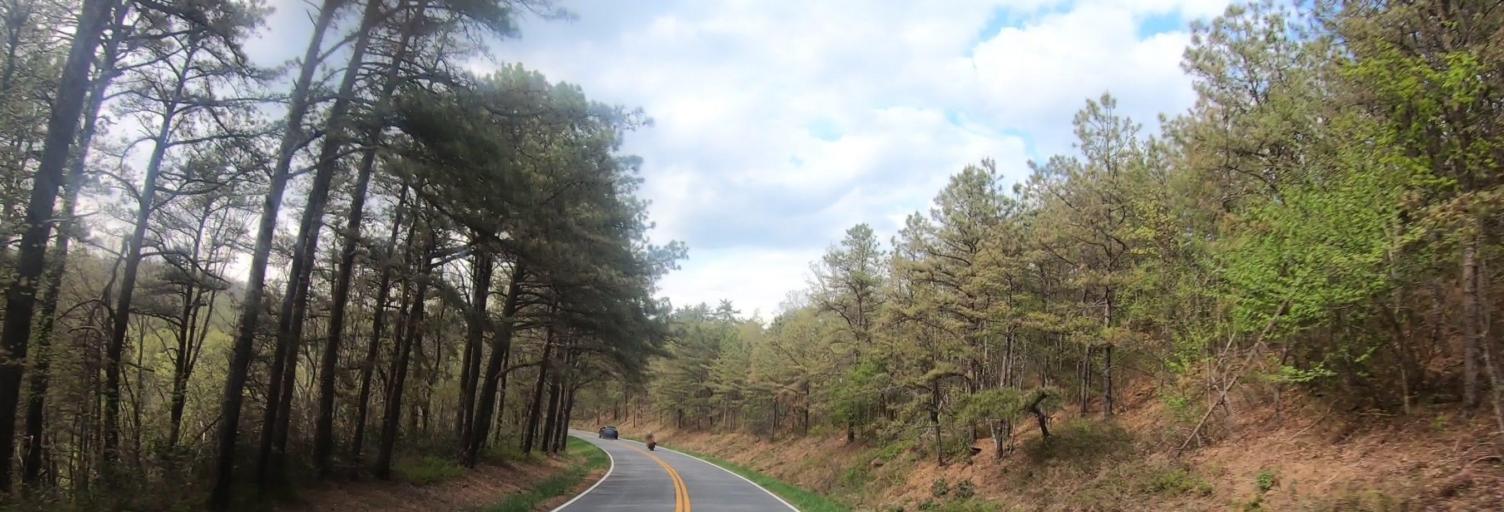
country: US
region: Virginia
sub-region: Augusta County
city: Dooms
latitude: 38.1111
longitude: -78.7825
